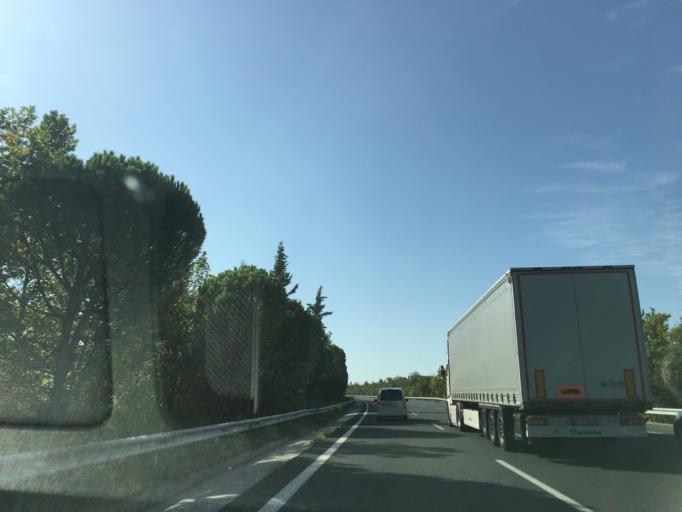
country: GR
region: Central Macedonia
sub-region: Nomos Pierias
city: Aiginio
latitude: 40.4934
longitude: 22.5643
